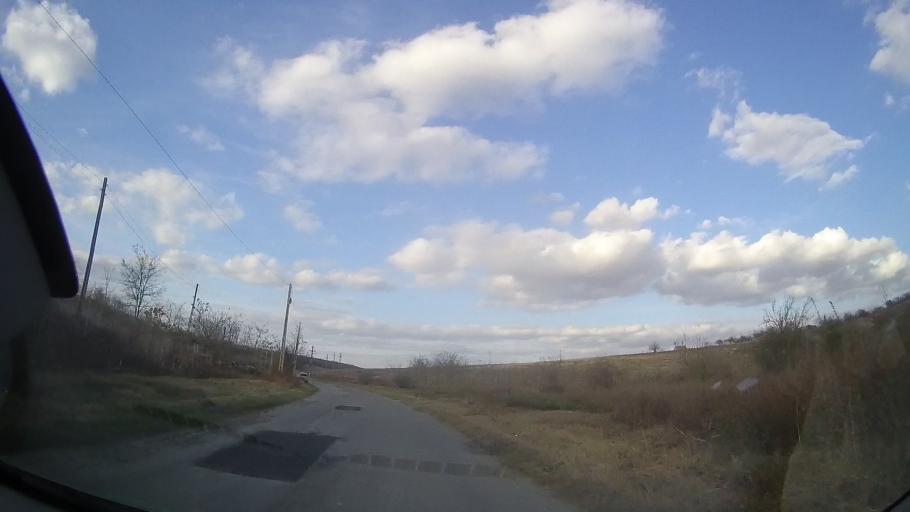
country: RO
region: Constanta
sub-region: Comuna Cerchezu
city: Cerchezu
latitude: 43.8271
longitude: 28.0978
